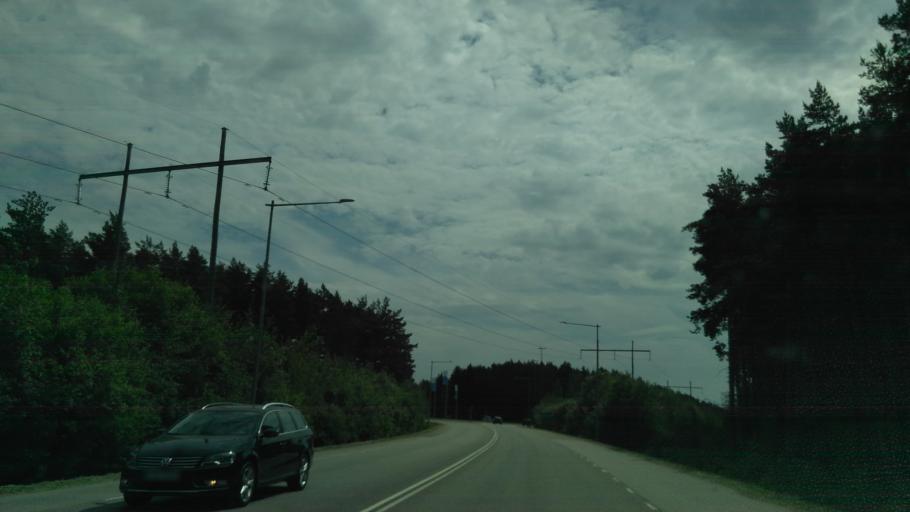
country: SE
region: Vaestra Goetaland
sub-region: Lidkopings Kommun
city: Lidkoping
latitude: 58.4906
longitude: 13.1838
